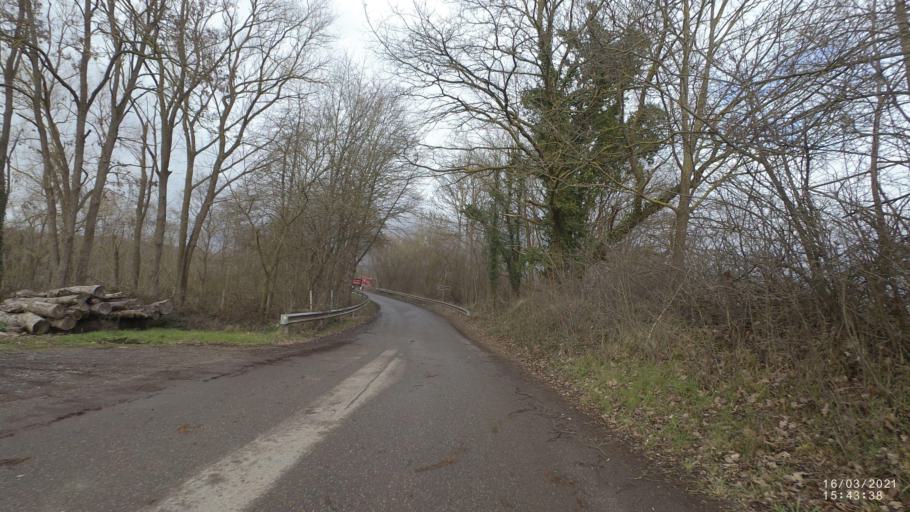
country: DE
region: Rheinland-Pfalz
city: Mendig
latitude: 50.3836
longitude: 7.2781
